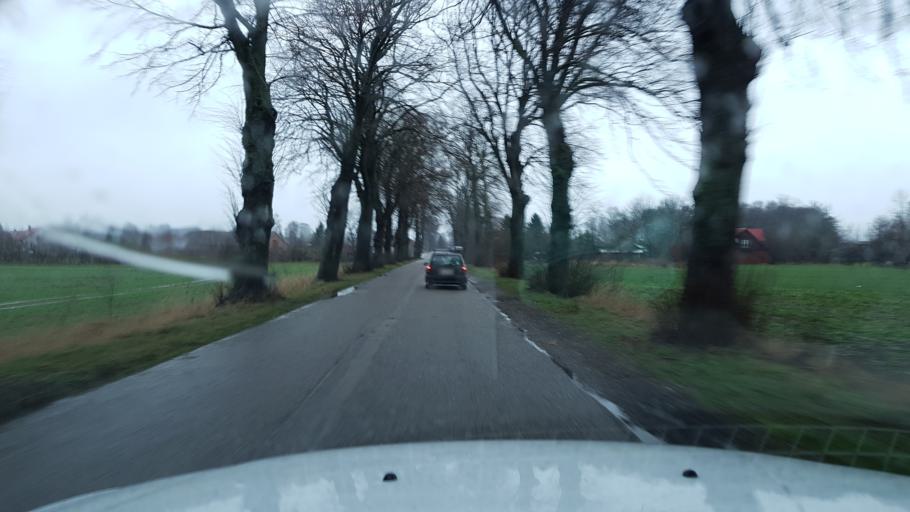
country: PL
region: West Pomeranian Voivodeship
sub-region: Powiat kolobrzeski
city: Ryman
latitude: 54.0126
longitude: 15.5139
